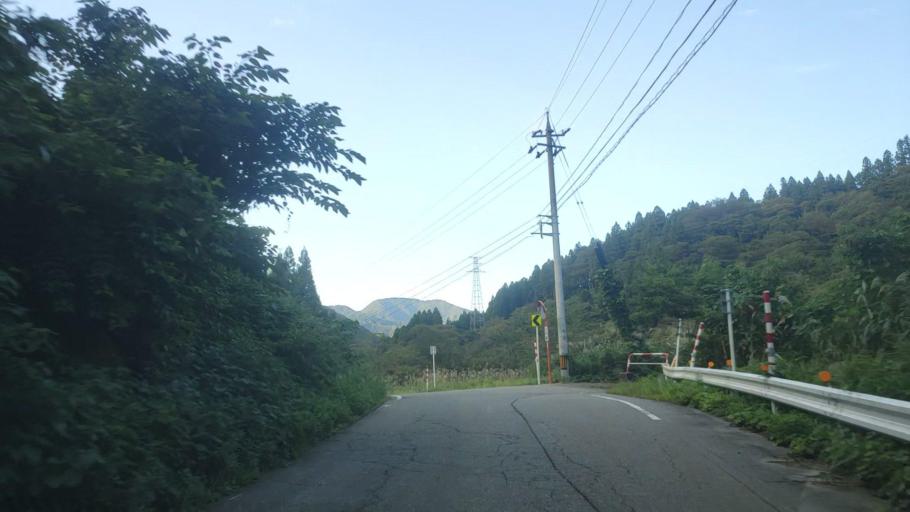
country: JP
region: Toyama
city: Yatsuomachi-higashikumisaka
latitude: 36.4905
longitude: 137.0638
